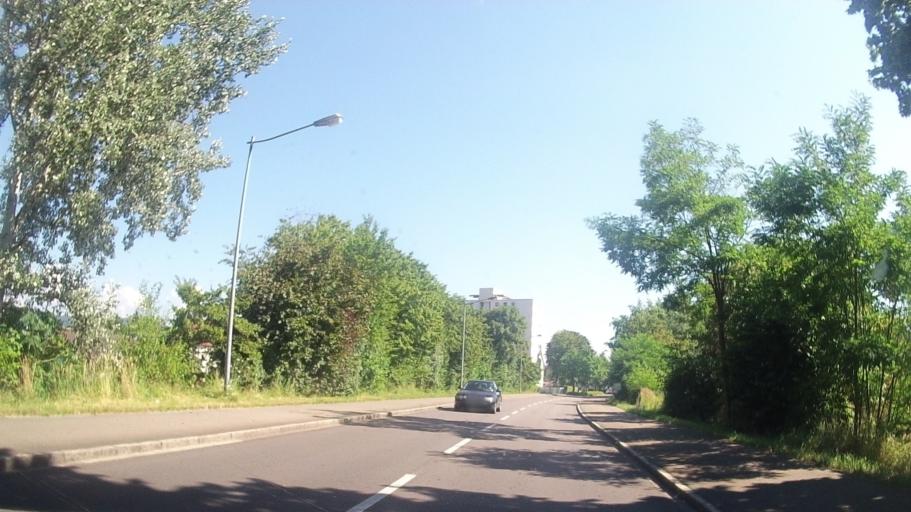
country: DE
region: Baden-Wuerttemberg
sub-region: Freiburg Region
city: Offenburg
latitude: 48.4835
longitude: 7.9391
